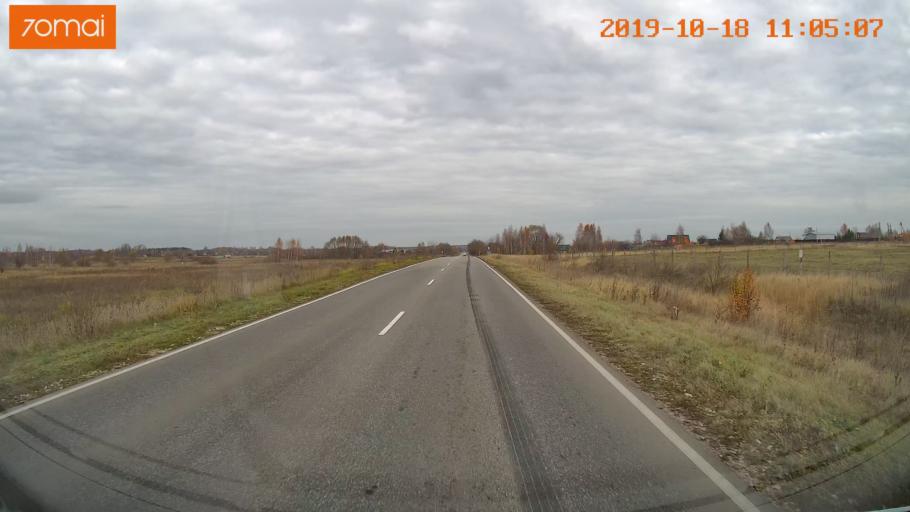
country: RU
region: Tula
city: Kimovsk
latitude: 53.9019
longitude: 38.5415
